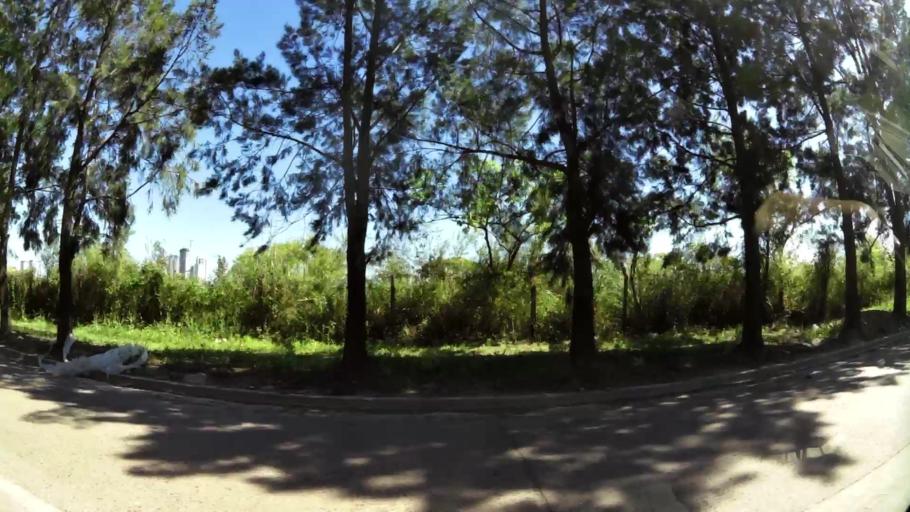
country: AR
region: Buenos Aires F.D.
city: Buenos Aires
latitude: -34.6239
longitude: -58.3483
